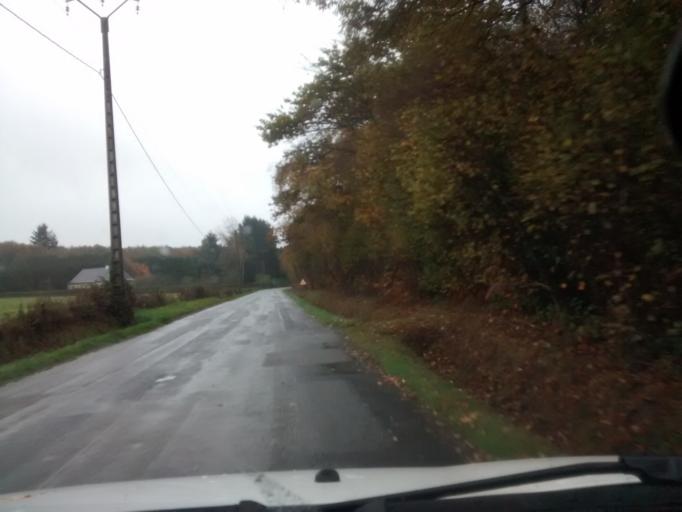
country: FR
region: Brittany
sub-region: Departement d'Ille-et-Vilaine
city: Chantepie
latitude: 48.0714
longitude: -1.6041
